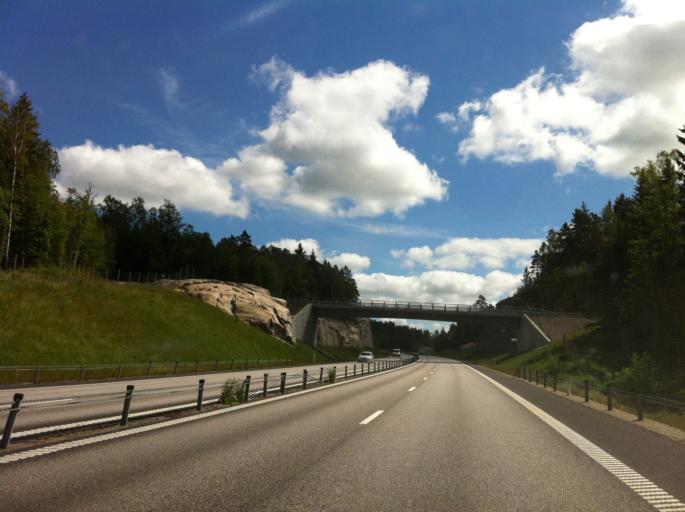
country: SE
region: Vaestra Goetaland
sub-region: Lilla Edets Kommun
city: Lodose
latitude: 58.0682
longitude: 12.1582
